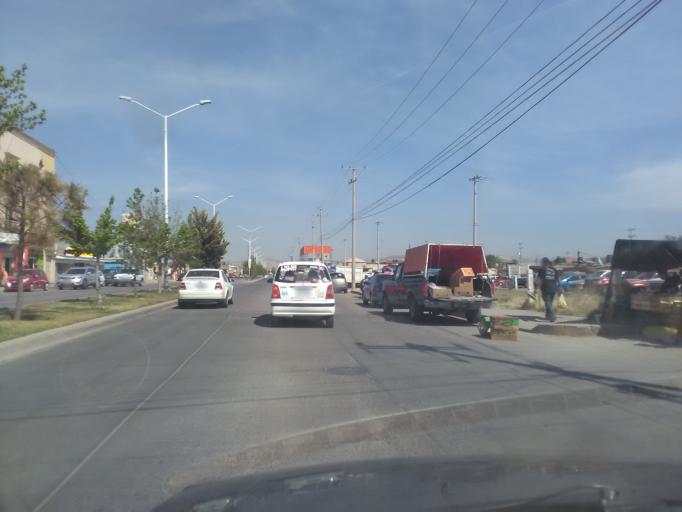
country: MX
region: Durango
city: Victoria de Durango
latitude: 24.0569
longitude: -104.6293
